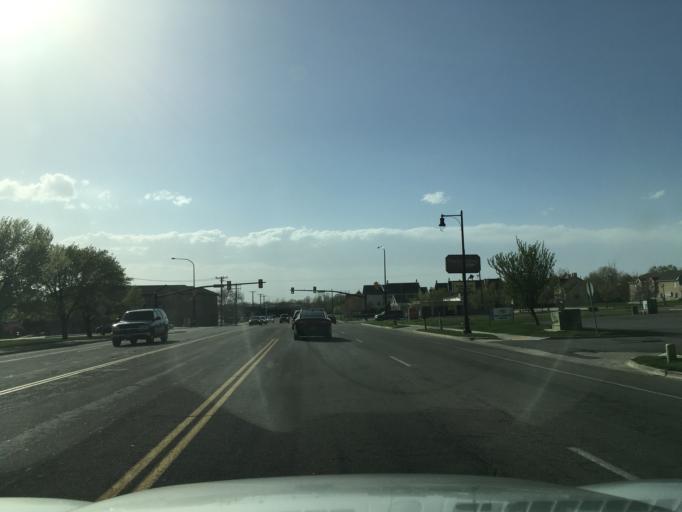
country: US
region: Utah
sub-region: Davis County
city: Kaysville
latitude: 41.0409
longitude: -111.9428
